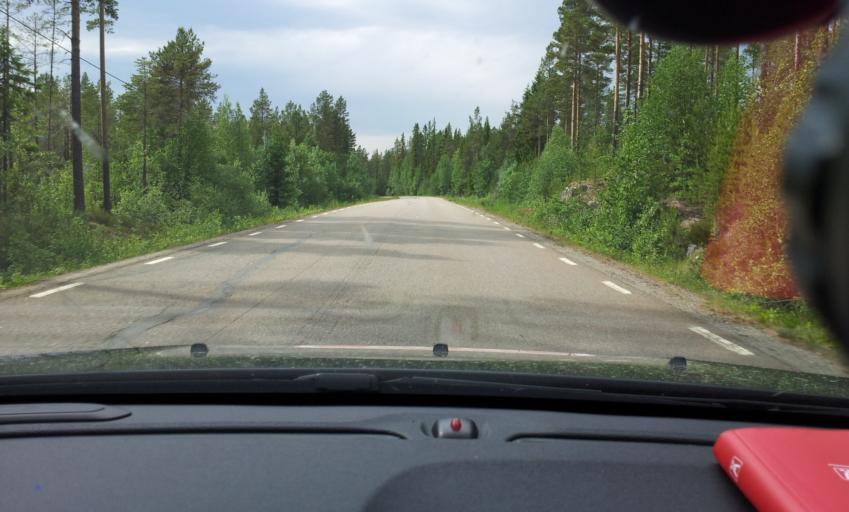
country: SE
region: Jaemtland
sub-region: Bergs Kommun
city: Hoverberg
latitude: 62.6611
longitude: 14.7766
